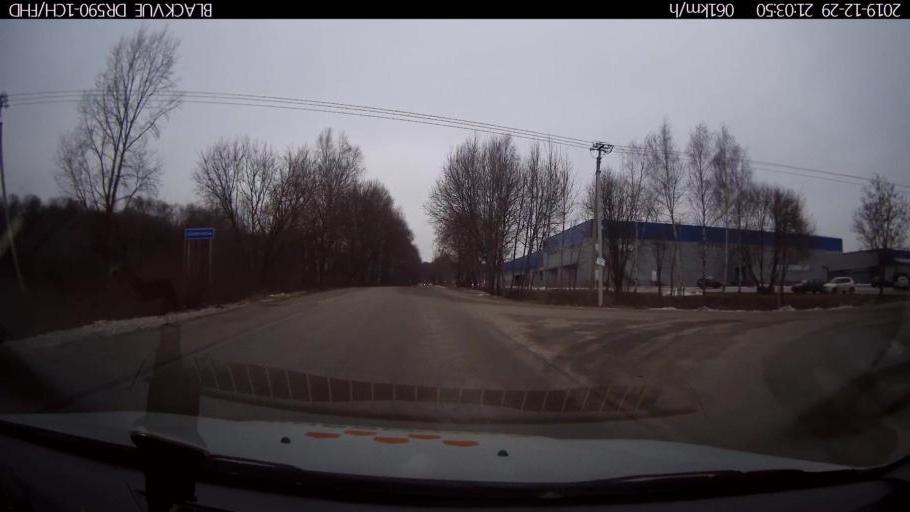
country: RU
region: Nizjnij Novgorod
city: Afonino
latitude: 56.1984
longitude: 44.0053
